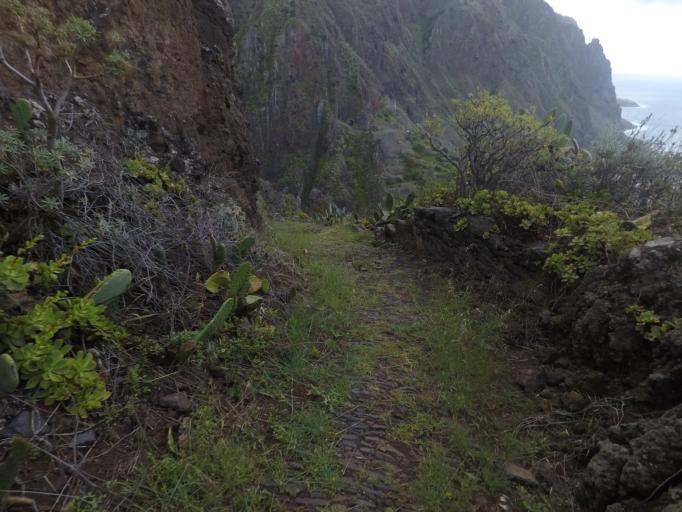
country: PT
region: Madeira
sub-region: Calheta
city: Faja da Ovelha
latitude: 32.7692
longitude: -17.2357
